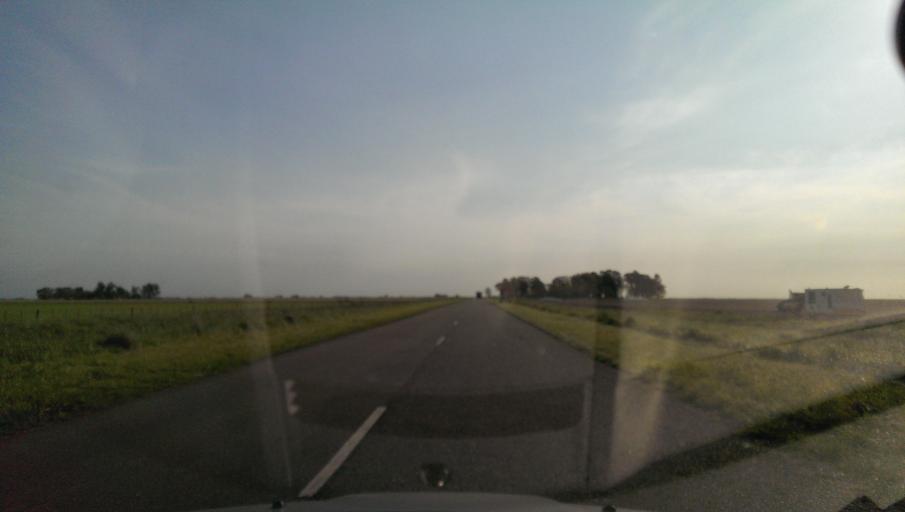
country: AR
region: Buenos Aires
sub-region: Partido de General La Madrid
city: General La Madrid
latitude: -37.4651
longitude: -61.1422
